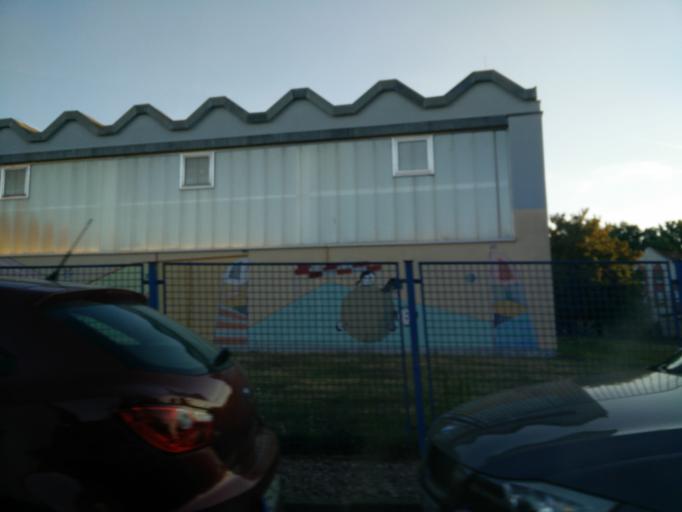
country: DE
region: Thuringia
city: Noda
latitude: 51.0198
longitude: 10.9940
